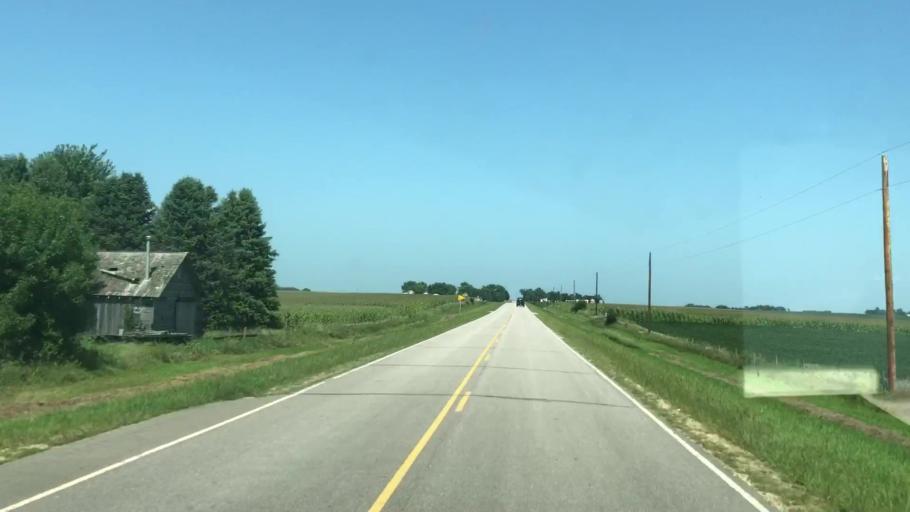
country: US
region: Iowa
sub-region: O'Brien County
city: Sanborn
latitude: 43.2501
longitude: -95.7234
